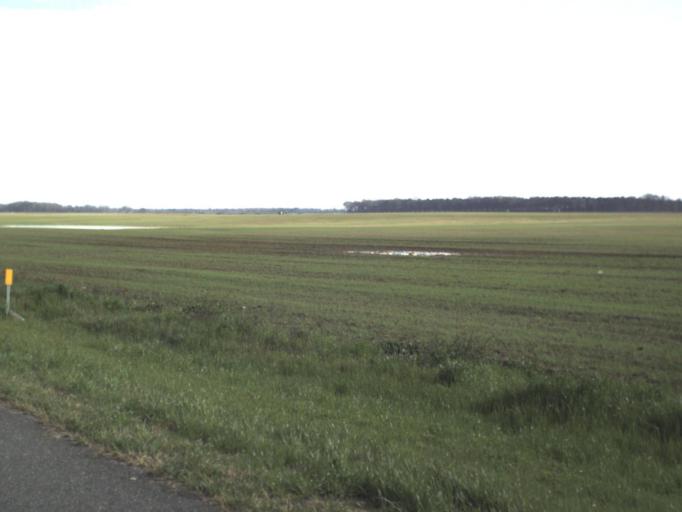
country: US
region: Florida
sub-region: Jackson County
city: Marianna
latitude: 30.8446
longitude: -85.1654
